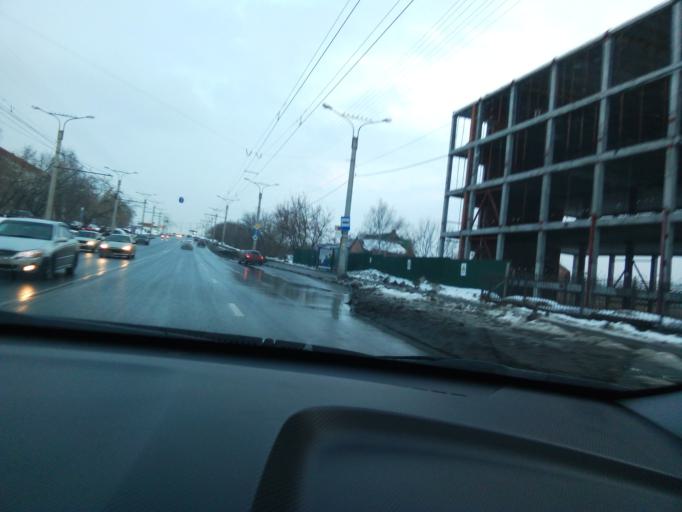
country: RU
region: Chuvashia
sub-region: Cheboksarskiy Rayon
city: Cheboksary
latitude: 56.1276
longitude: 47.2437
